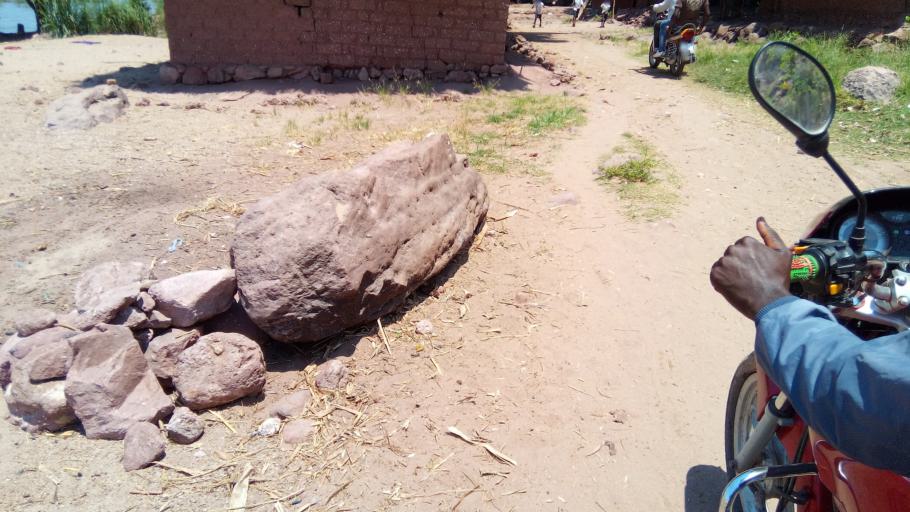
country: CD
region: Katanga
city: Kalemie
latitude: -5.9880
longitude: 29.1929
